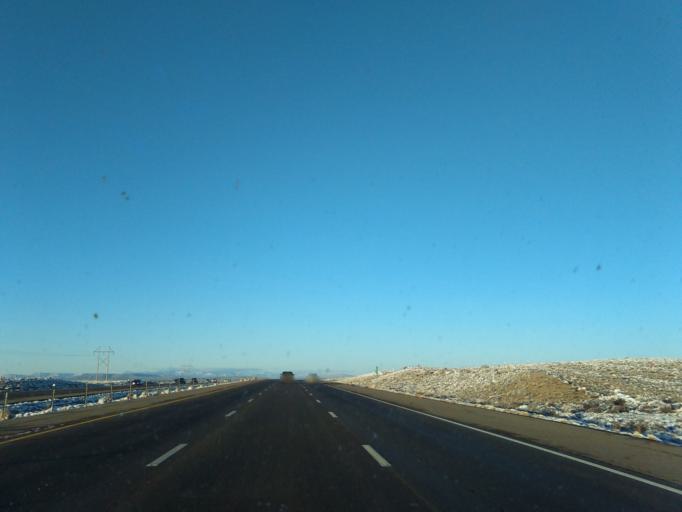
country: US
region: New Mexico
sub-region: Sandoval County
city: Corrales
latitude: 35.2305
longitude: -106.5708
